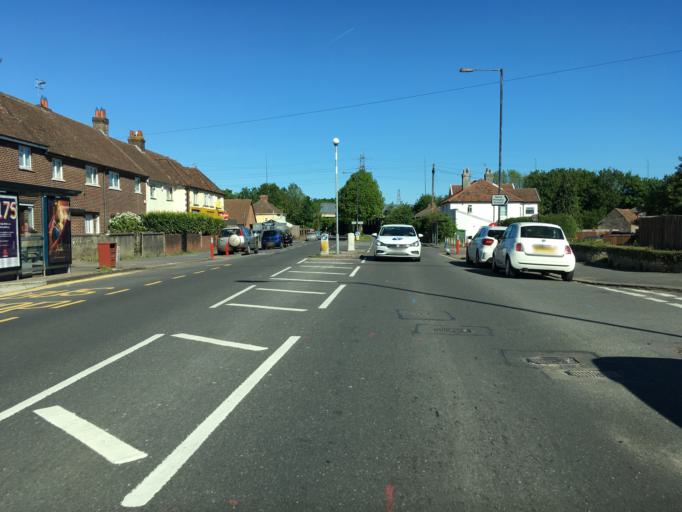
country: GB
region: England
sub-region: North Somerset
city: Easton-in-Gordano
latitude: 51.4949
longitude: -2.6828
